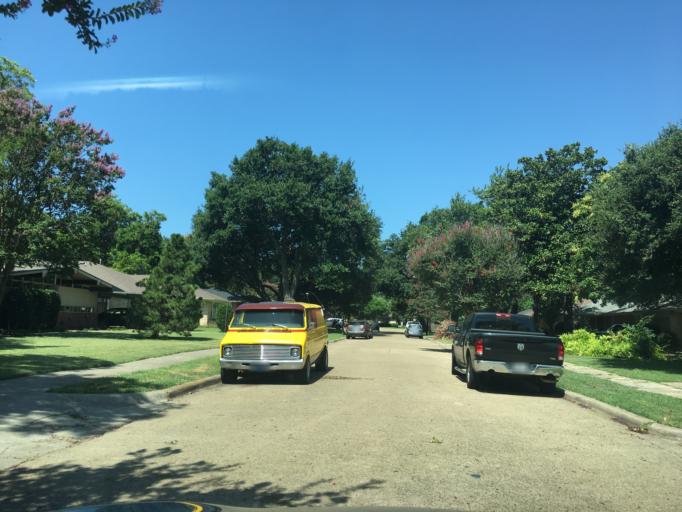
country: US
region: Texas
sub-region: Dallas County
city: Highland Park
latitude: 32.8432
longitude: -96.7446
